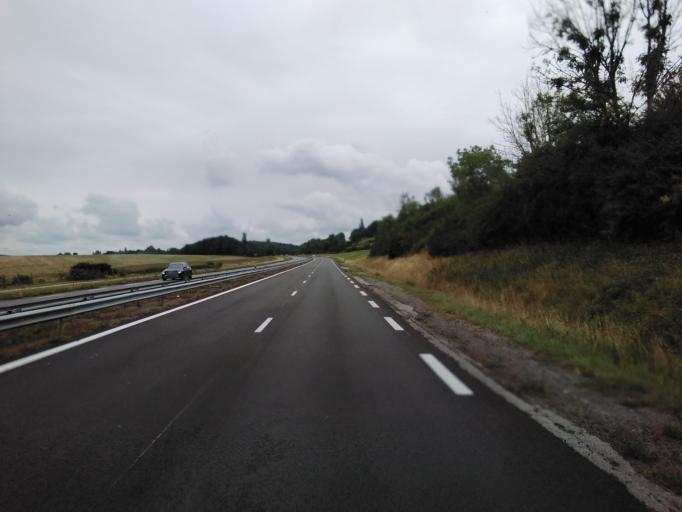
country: FR
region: Franche-Comte
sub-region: Departement du Jura
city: Lons-le-Saunier
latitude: 46.7280
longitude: 5.5579
